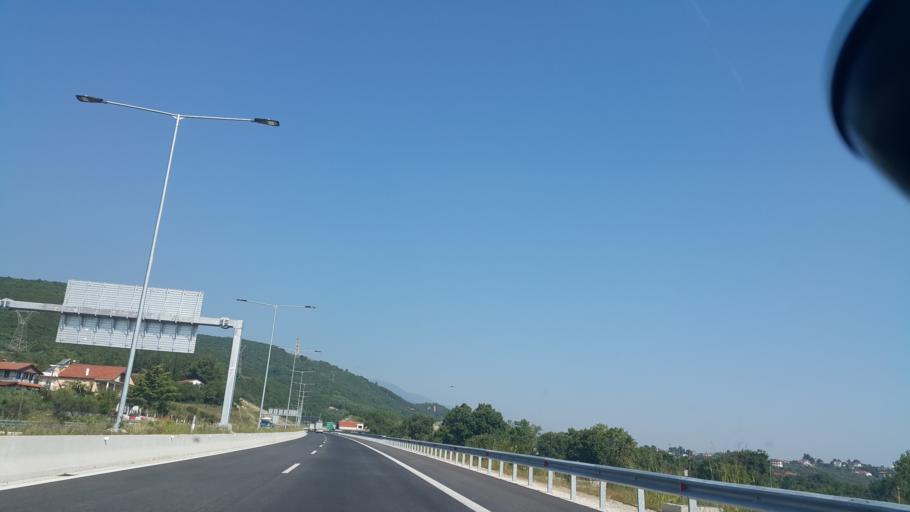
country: GR
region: Thessaly
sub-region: Nomos Larisis
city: Pyrgetos
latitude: 39.9826
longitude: 22.6177
